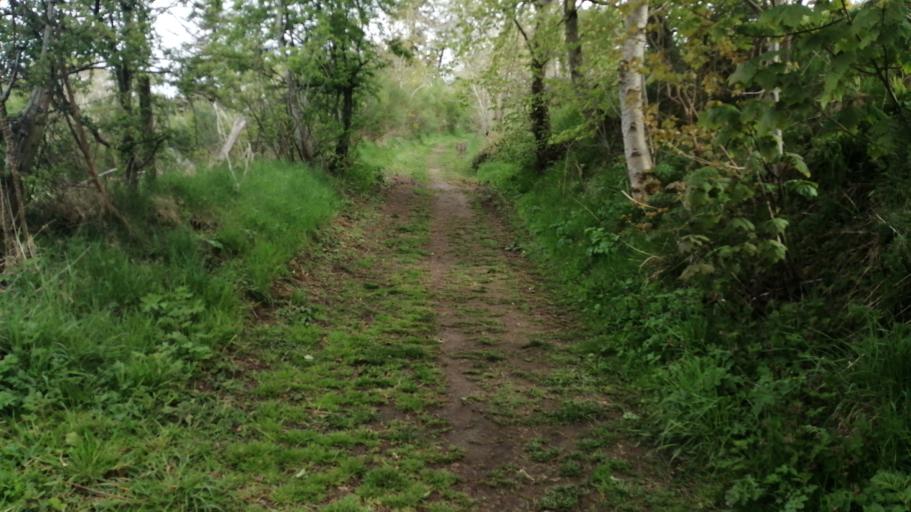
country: GB
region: Scotland
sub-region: Moray
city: Keith
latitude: 57.5314
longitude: -2.9627
